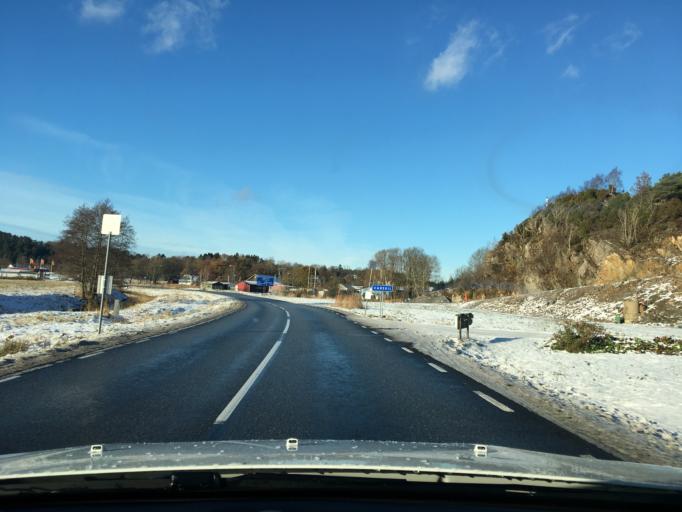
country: SE
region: Vaestra Goetaland
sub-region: Tjorns Kommun
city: Myggenas
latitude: 58.1237
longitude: 11.7284
